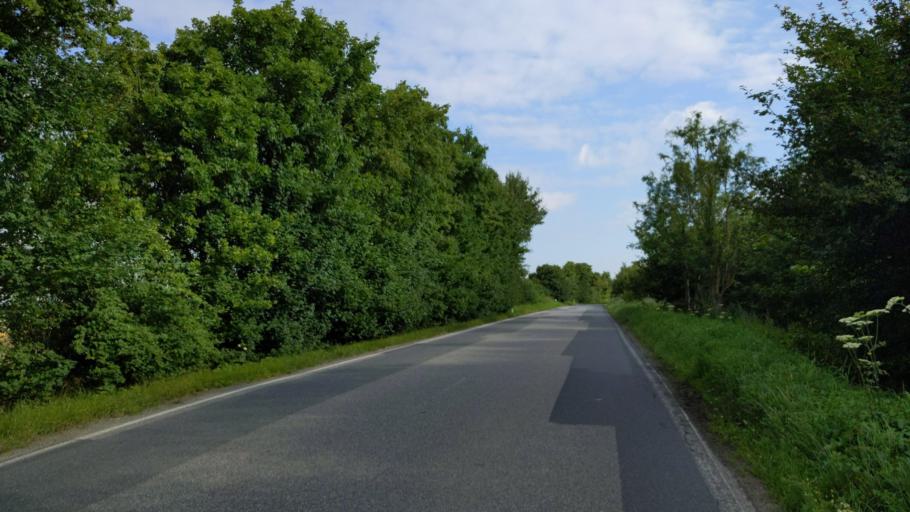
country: DE
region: Schleswig-Holstein
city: Bad Schwartau
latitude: 53.9859
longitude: 10.6607
